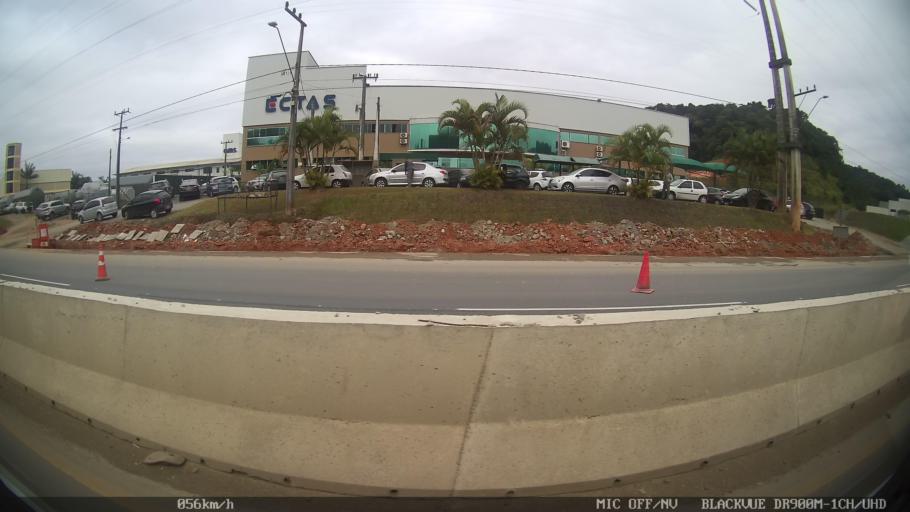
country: BR
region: Santa Catarina
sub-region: Joinville
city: Joinville
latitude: -26.2543
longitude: -48.8890
